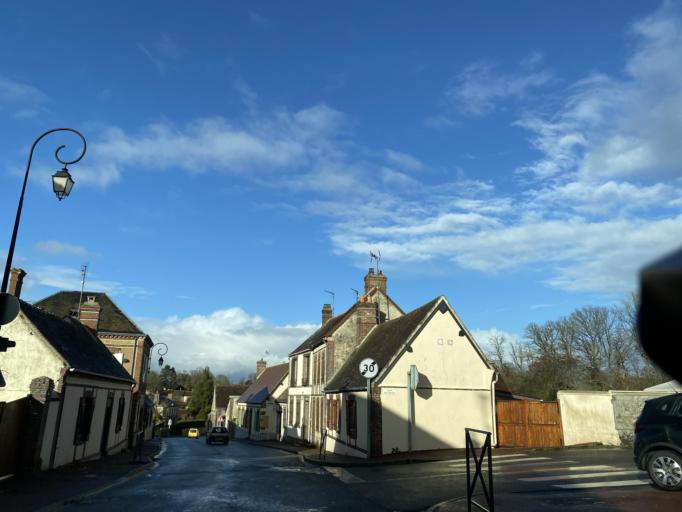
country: FR
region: Centre
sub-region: Departement d'Eure-et-Loir
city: Brezolles
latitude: 48.6287
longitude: 1.1491
